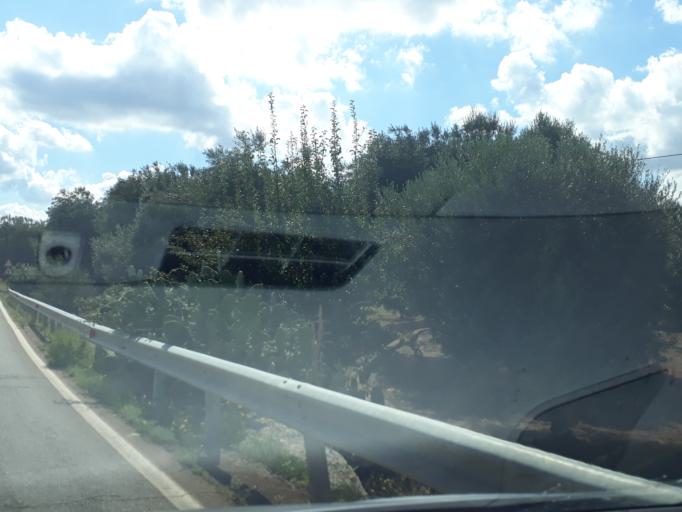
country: IT
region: Apulia
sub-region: Provincia di Brindisi
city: Fasano
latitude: 40.8205
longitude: 17.3767
